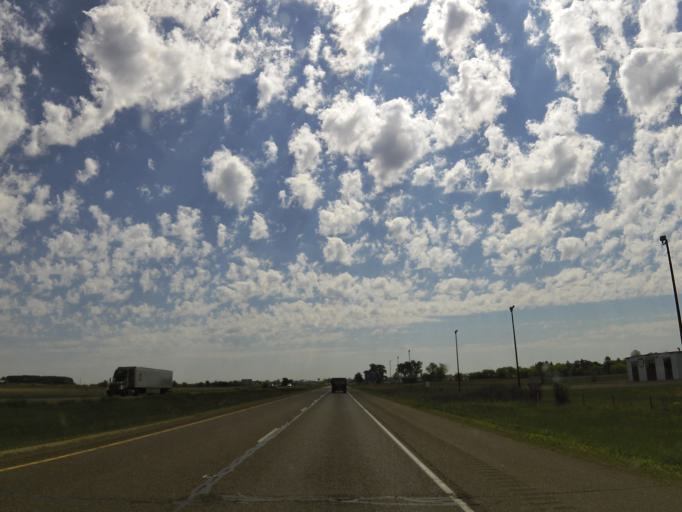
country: US
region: Wisconsin
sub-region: Eau Claire County
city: Eau Claire
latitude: 44.8480
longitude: -91.6235
